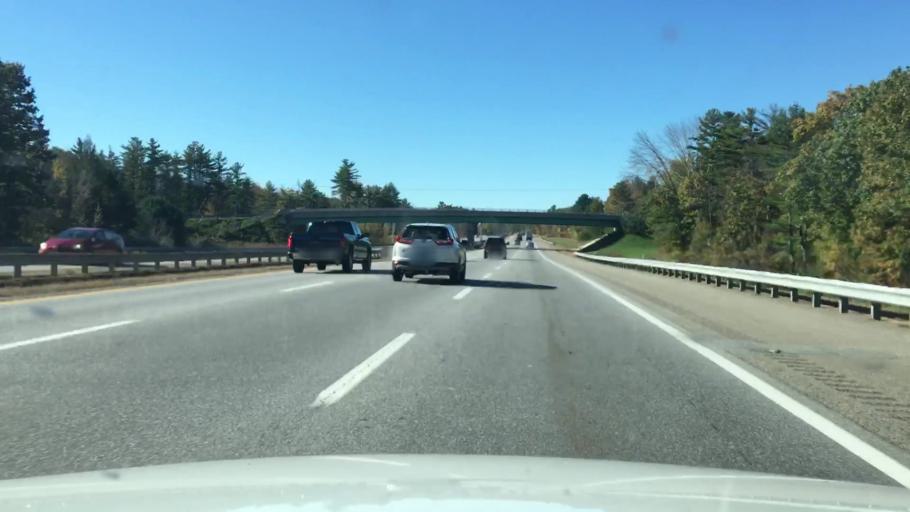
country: US
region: Maine
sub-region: York County
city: Biddeford
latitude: 43.4689
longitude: -70.5143
